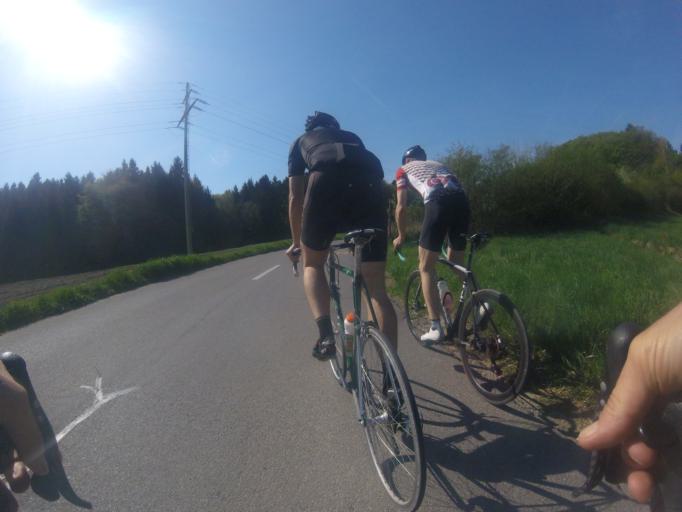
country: CH
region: Bern
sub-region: Bern-Mittelland District
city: Muhleberg
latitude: 46.9820
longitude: 7.2396
